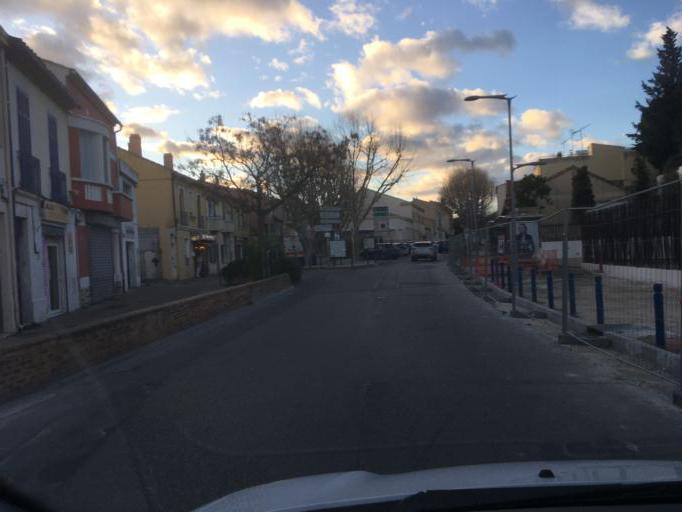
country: FR
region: Provence-Alpes-Cote d'Azur
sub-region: Departement des Bouches-du-Rhone
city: Martigues
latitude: 43.4079
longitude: 5.0535
